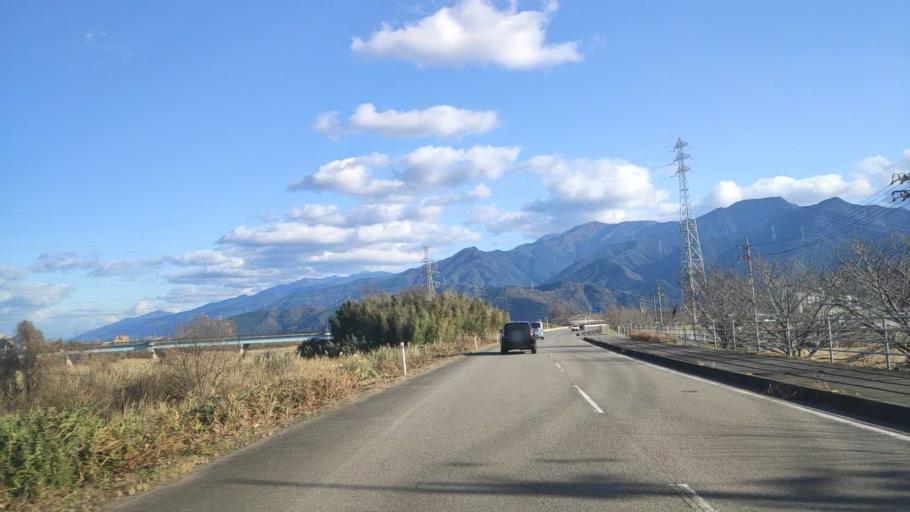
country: JP
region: Ehime
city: Saijo
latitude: 33.9102
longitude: 133.1670
